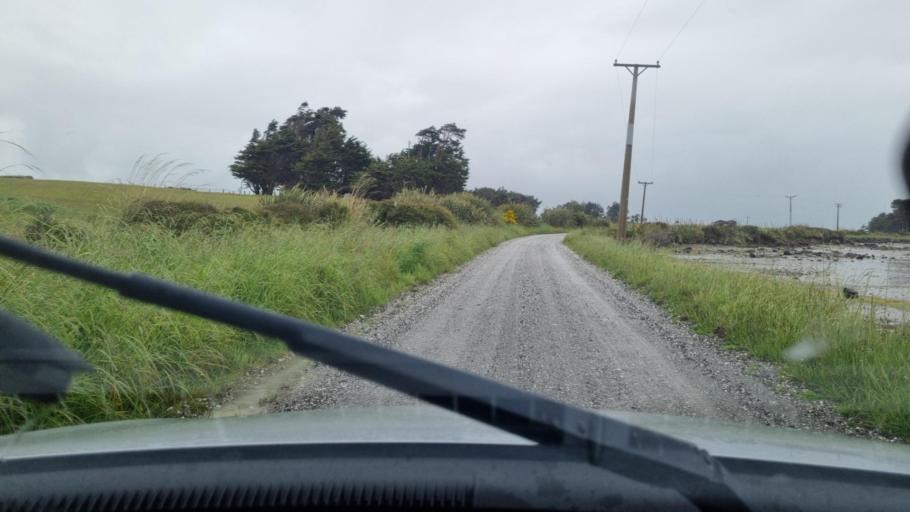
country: NZ
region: Southland
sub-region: Invercargill City
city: Bluff
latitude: -46.5492
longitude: 168.3057
